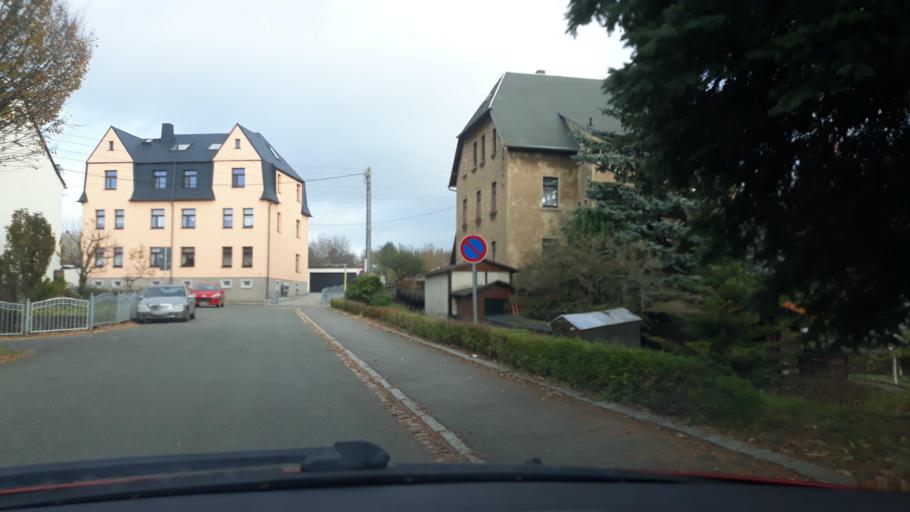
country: DE
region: Saxony
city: Reinsdorf
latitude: 50.6818
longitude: 12.5612
